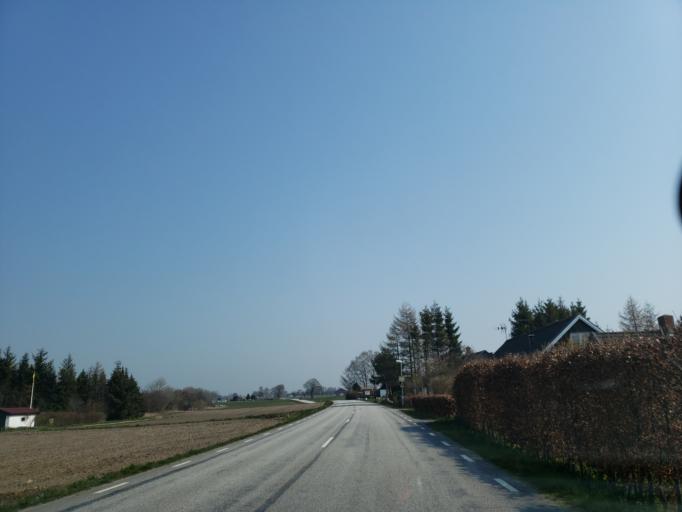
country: SE
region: Skane
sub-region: Simrishamns Kommun
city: Simrishamn
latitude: 55.4665
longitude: 14.2089
